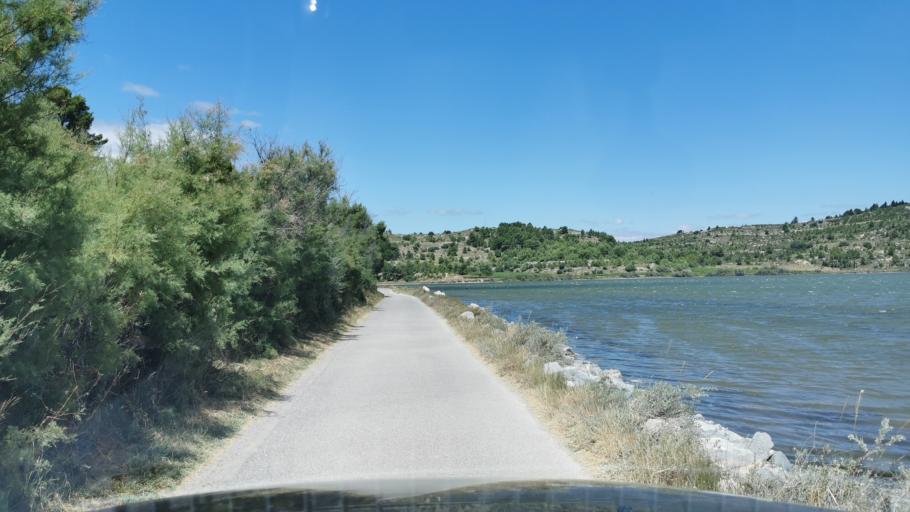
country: FR
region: Languedoc-Roussillon
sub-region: Departement de l'Aude
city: Peyriac-de-Mer
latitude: 43.0876
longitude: 2.9727
